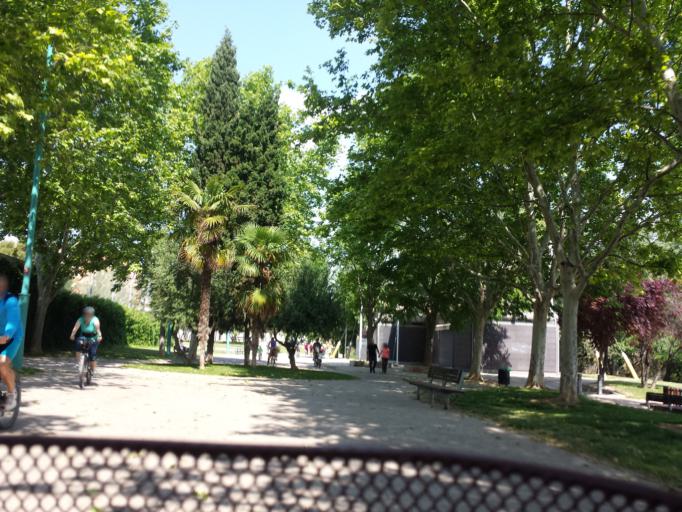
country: ES
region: Aragon
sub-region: Provincia de Zaragoza
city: Almozara
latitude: 41.6619
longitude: -0.8936
